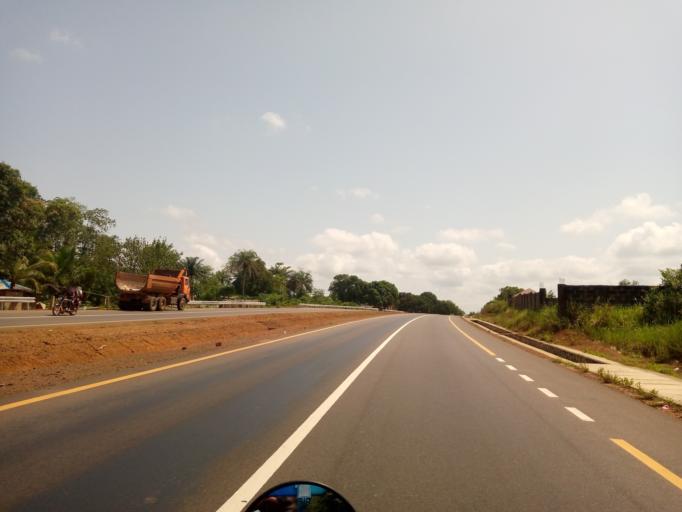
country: SL
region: Western Area
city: Waterloo
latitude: 8.3776
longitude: -12.9584
